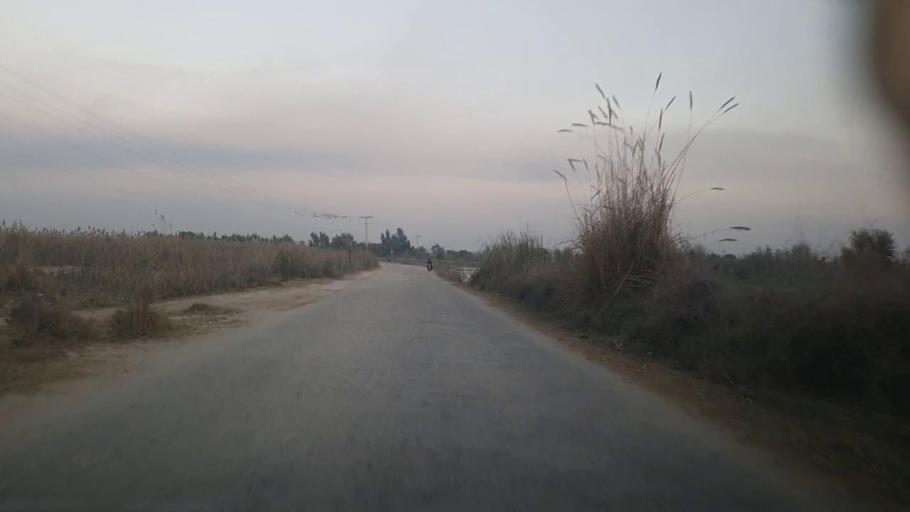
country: PK
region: Sindh
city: Kandiari
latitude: 26.6823
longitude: 68.9402
